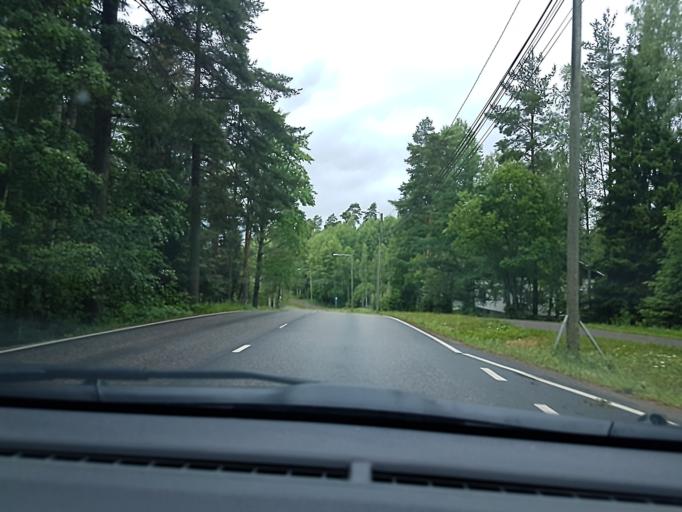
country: FI
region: Uusimaa
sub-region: Helsinki
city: Pornainen
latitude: 60.4719
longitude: 25.3812
